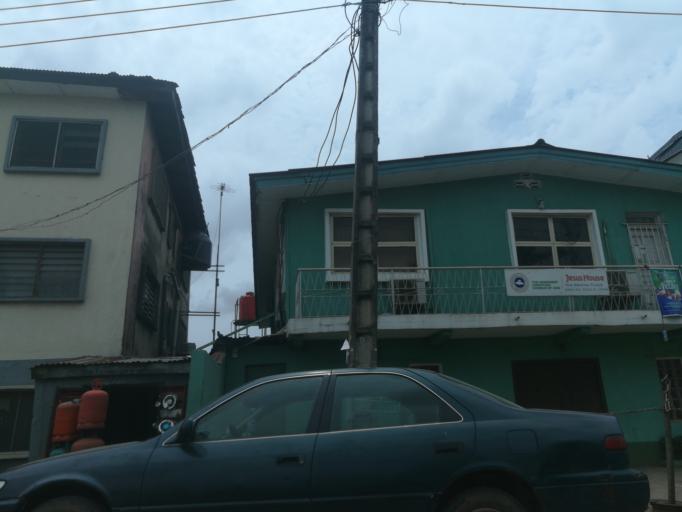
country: NG
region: Lagos
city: Somolu
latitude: 6.5339
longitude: 3.3909
